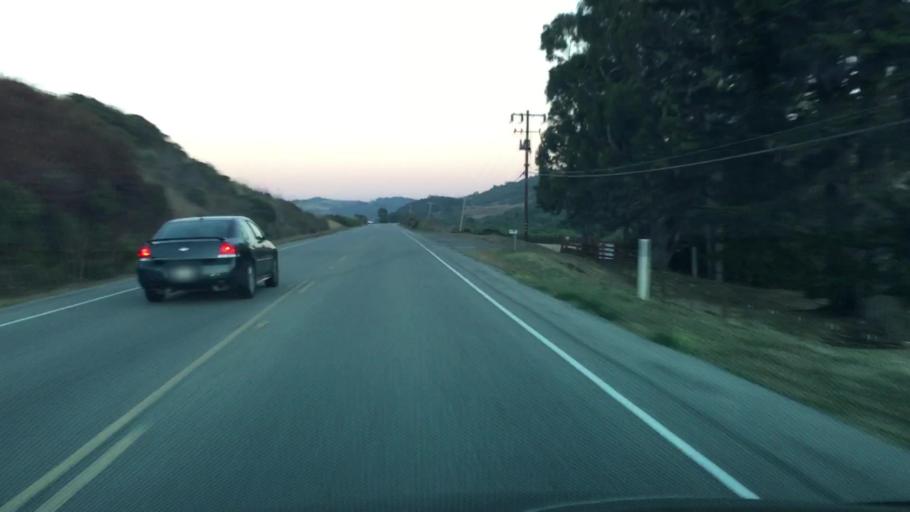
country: US
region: California
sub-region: San Mateo County
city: Half Moon Bay
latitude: 37.3307
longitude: -122.3759
